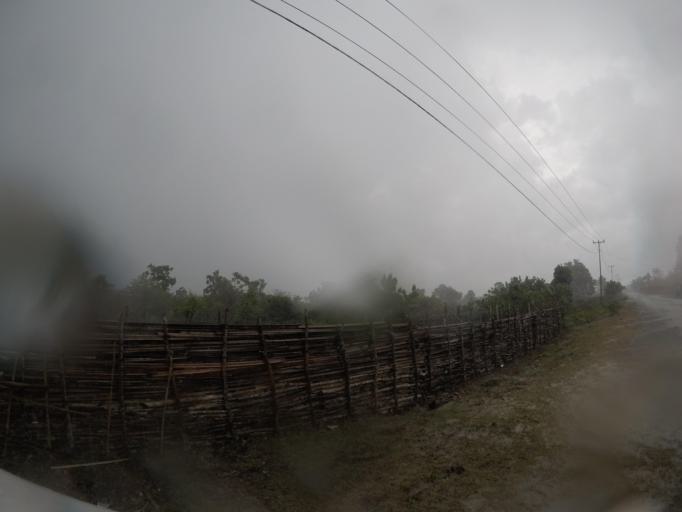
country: TL
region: Bobonaro
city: Maliana
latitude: -8.8662
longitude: 125.1038
